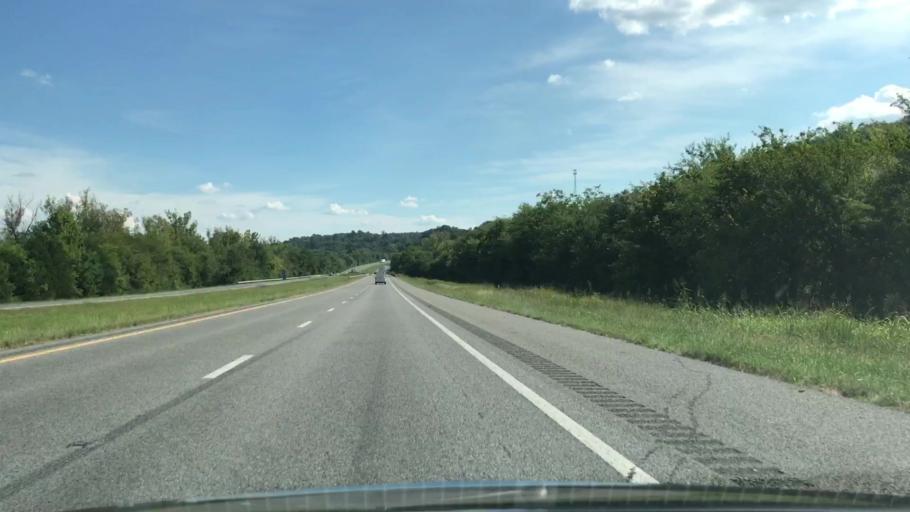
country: US
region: Alabama
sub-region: Limestone County
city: Ardmore
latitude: 35.1344
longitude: -86.8780
